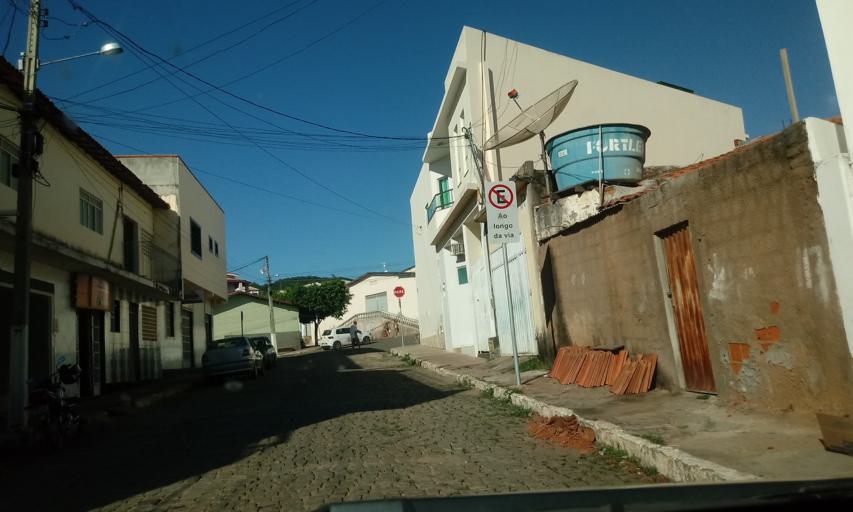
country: BR
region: Bahia
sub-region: Riacho De Santana
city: Riacho de Santana
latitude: -13.7712
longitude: -42.7159
